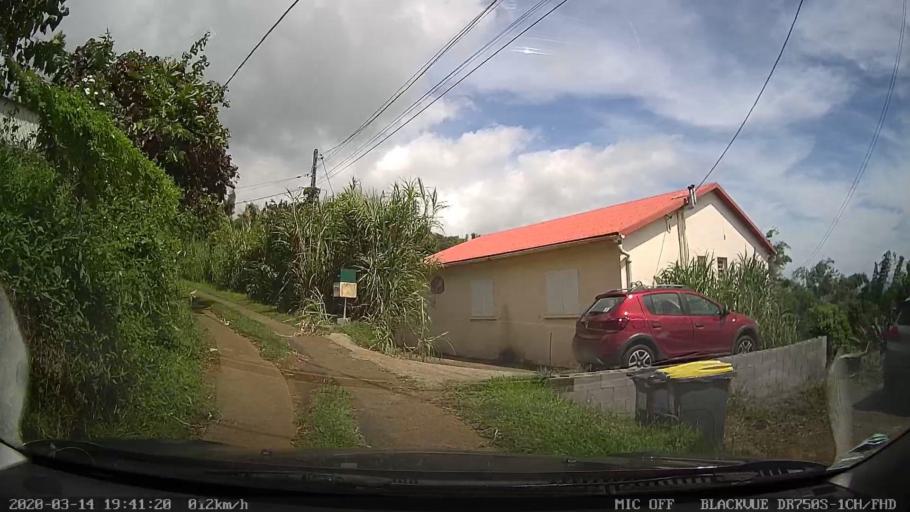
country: RE
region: Reunion
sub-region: Reunion
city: Sainte-Marie
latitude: -20.9464
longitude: 55.5261
